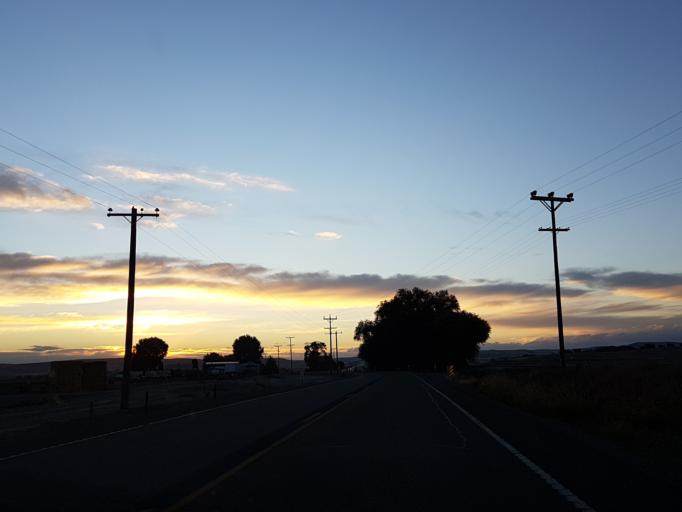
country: US
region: Oregon
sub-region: Malheur County
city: Vale
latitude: 43.9387
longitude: -117.3315
